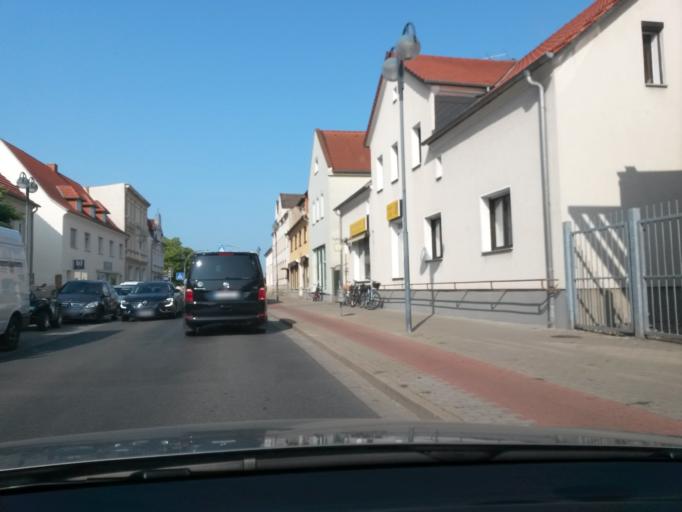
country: DE
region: Saxony-Anhalt
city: Tangerhutte
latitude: 52.4347
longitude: 11.8130
